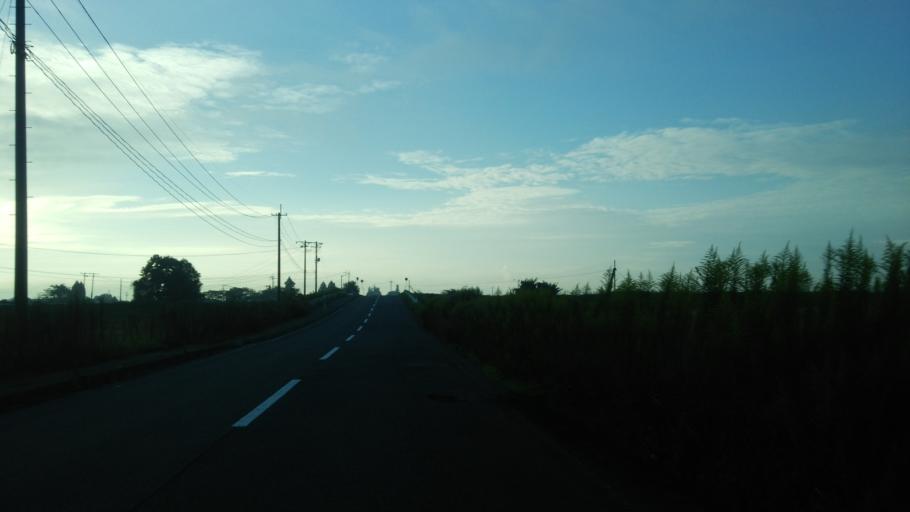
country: JP
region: Fukushima
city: Kitakata
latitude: 37.5505
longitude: 139.8532
